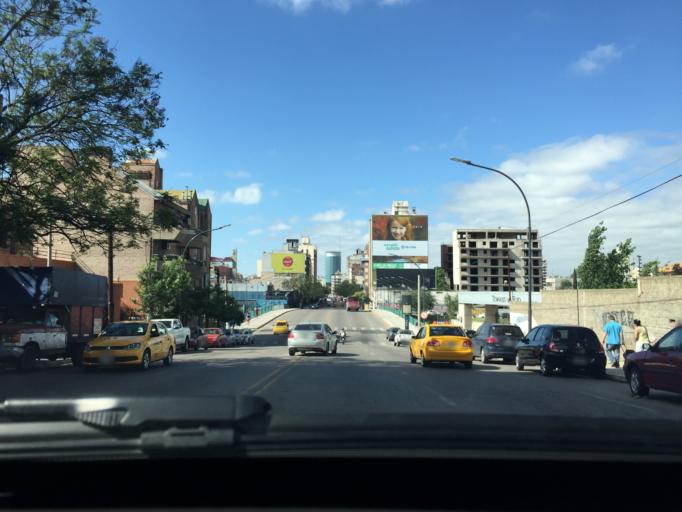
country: AR
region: Cordoba
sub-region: Departamento de Capital
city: Cordoba
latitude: -31.4038
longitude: -64.1989
